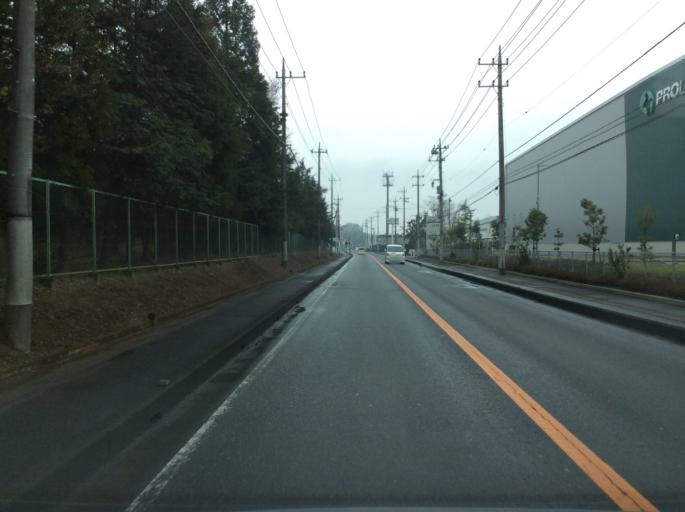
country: JP
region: Ibaraki
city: Mitsukaido
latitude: 35.9862
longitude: 139.9471
